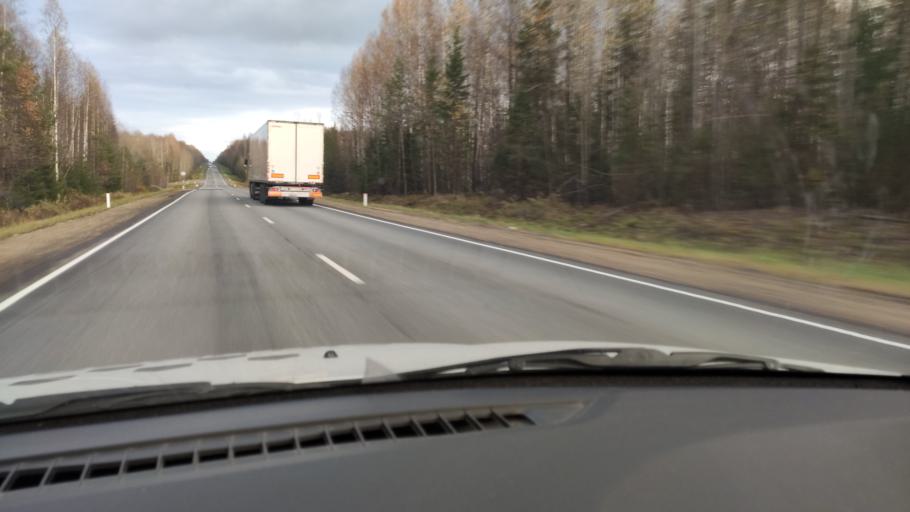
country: RU
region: Kirov
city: Chernaya Kholunitsa
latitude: 58.7737
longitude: 51.9396
